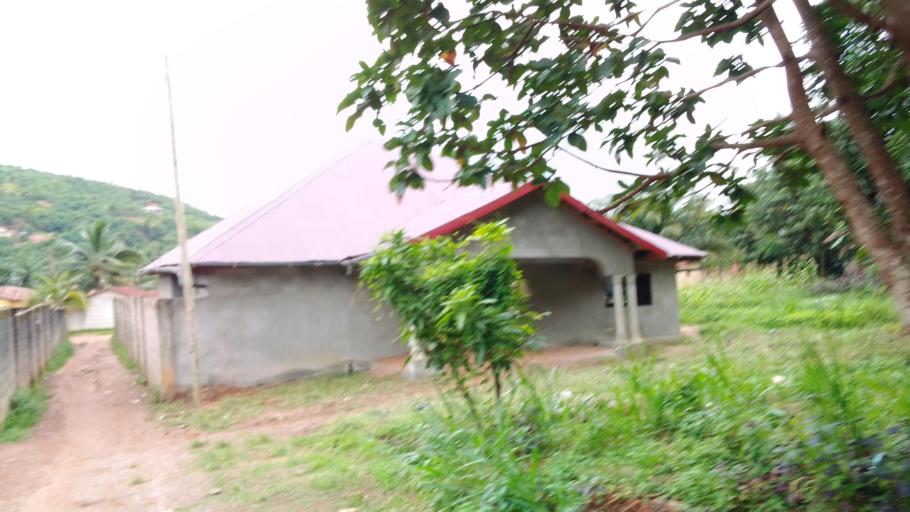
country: SL
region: Eastern Province
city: Kenema
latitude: 7.8548
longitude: -11.1941
